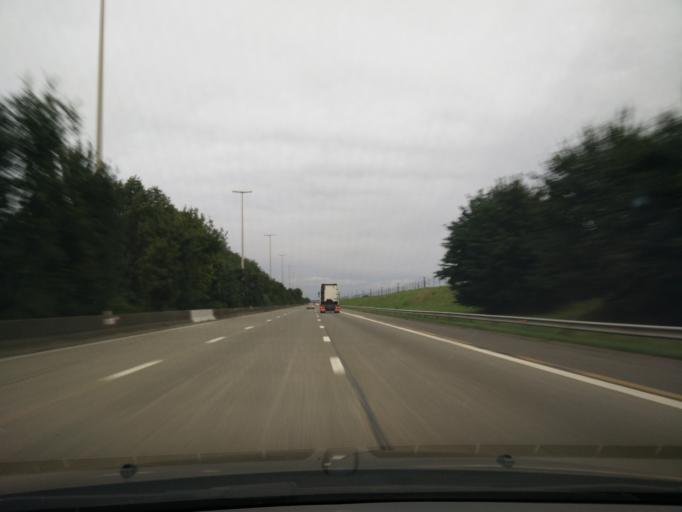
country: BE
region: Flanders
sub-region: Provincie Limburg
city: Gingelom
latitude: 50.7061
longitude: 5.1174
